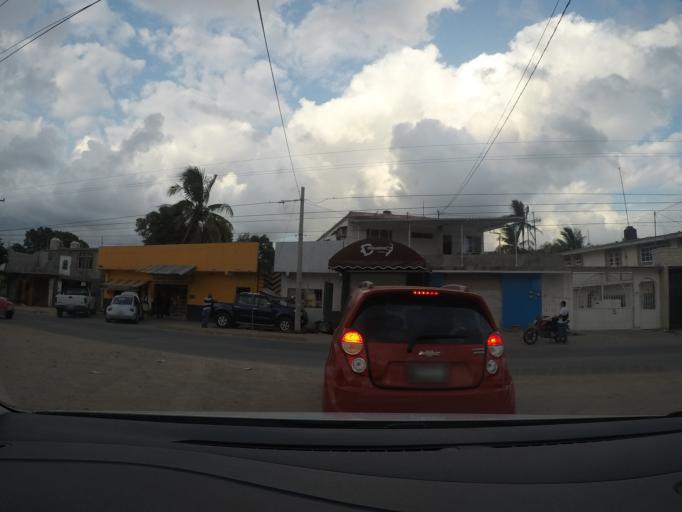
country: MX
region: Oaxaca
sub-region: Salina Cruz
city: Salina Cruz
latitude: 16.2069
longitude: -95.1968
